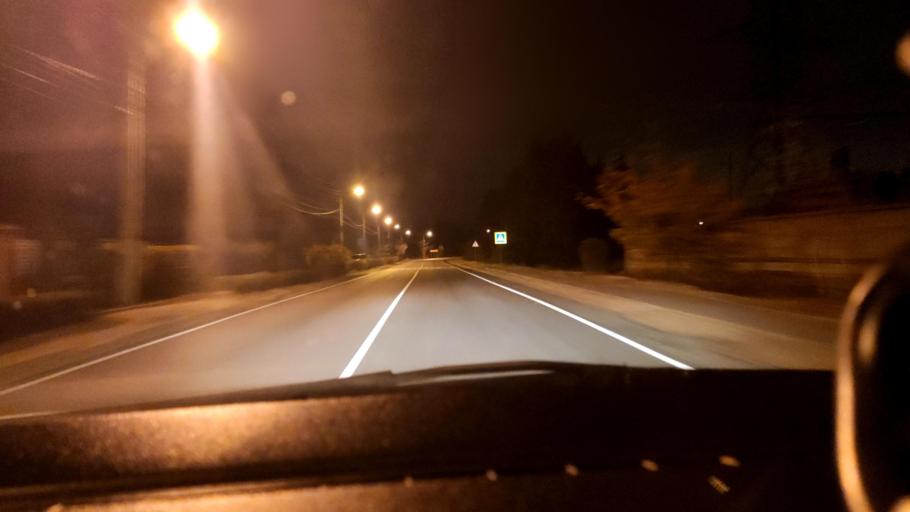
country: RU
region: Voronezj
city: Shilovo
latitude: 51.6015
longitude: 39.0343
